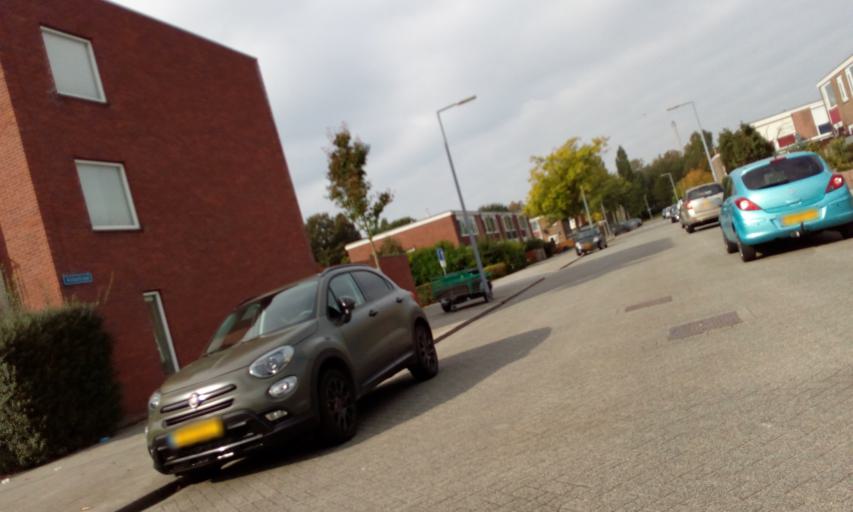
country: NL
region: South Holland
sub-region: Gemeente Spijkenisse
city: Spijkenisse
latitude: 51.8723
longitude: 4.3615
